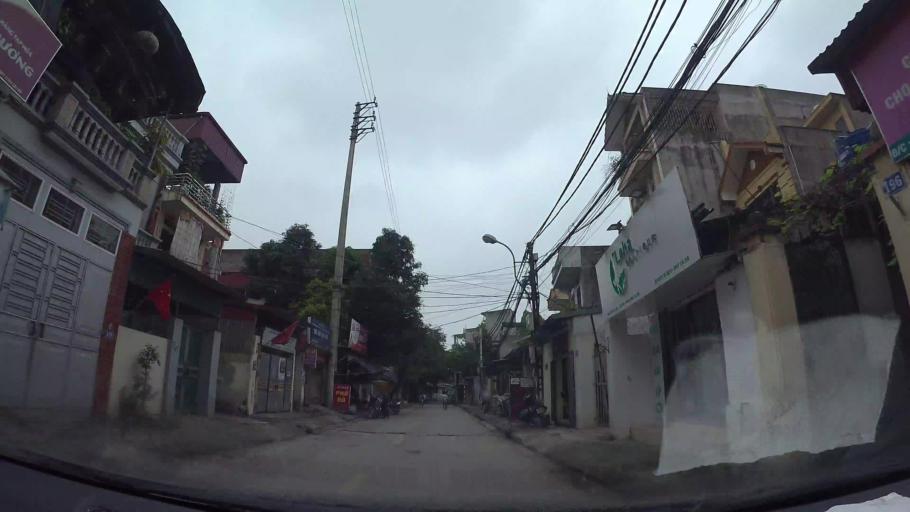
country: VN
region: Hung Yen
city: Van Giang
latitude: 20.9711
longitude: 105.8937
